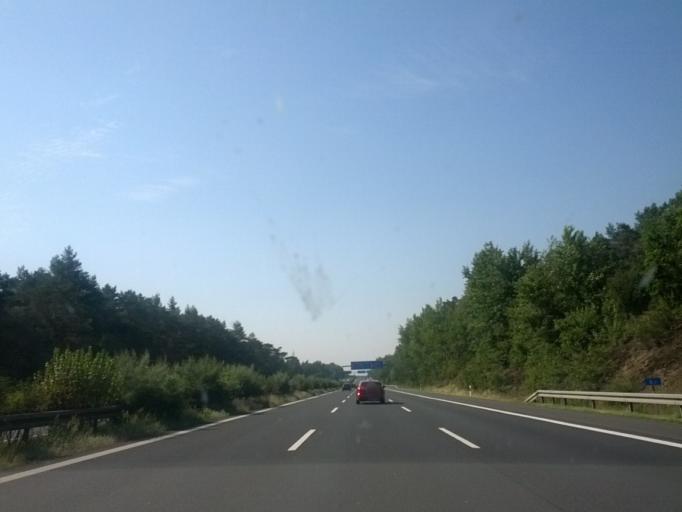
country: DE
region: Brandenburg
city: Borkheide
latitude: 52.2219
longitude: 12.9063
